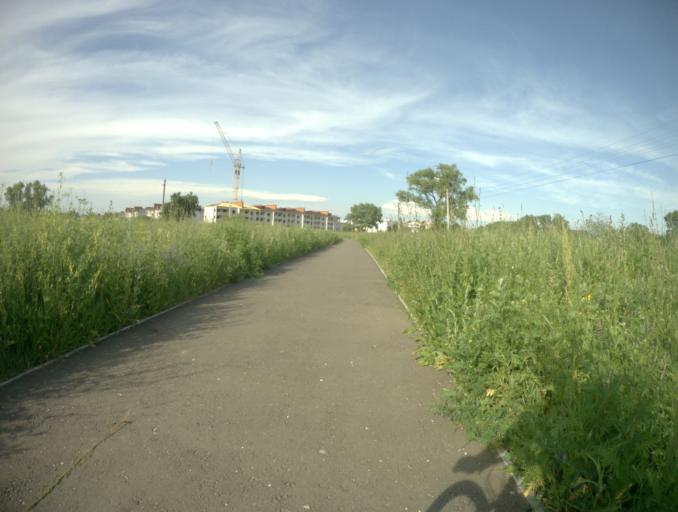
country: RU
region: Vladimir
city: Suzdal'
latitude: 56.4310
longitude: 40.4505
